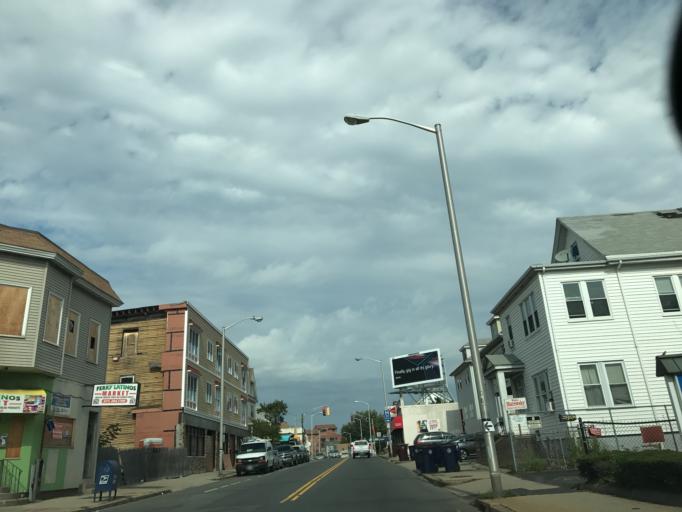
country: US
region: Massachusetts
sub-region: Middlesex County
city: Everett
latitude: 42.4077
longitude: -71.0466
